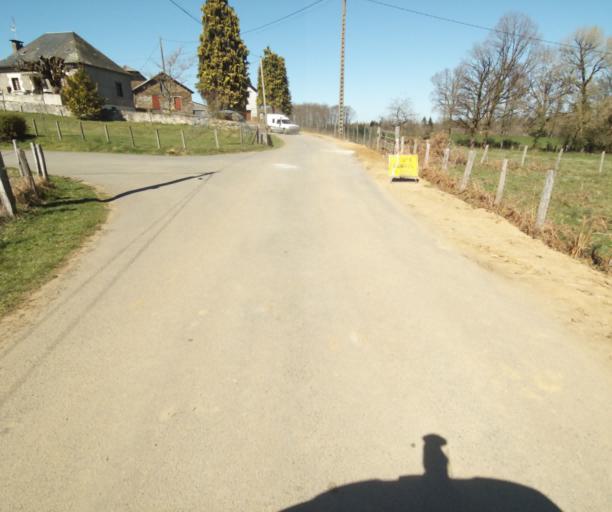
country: FR
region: Limousin
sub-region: Departement de la Correze
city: Saint-Clement
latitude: 45.3727
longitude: 1.6816
